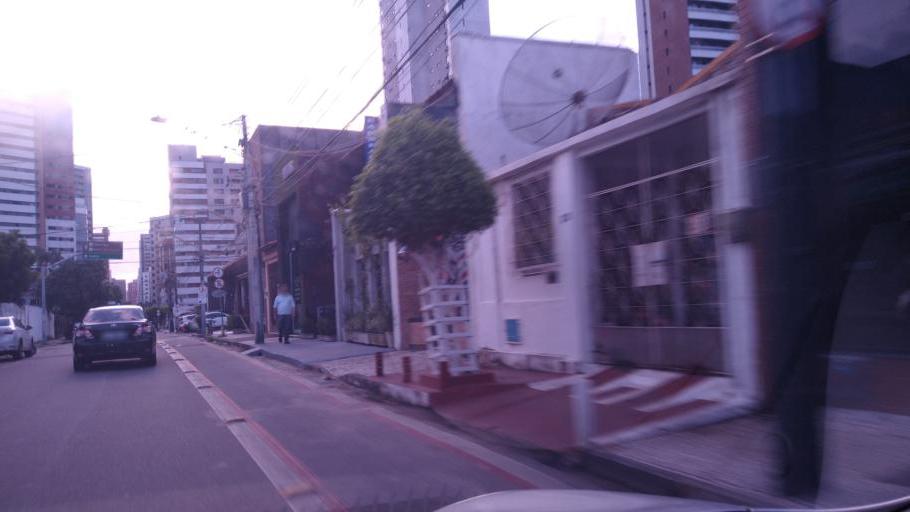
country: BR
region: Ceara
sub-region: Fortaleza
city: Fortaleza
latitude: -3.7313
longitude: -38.4899
